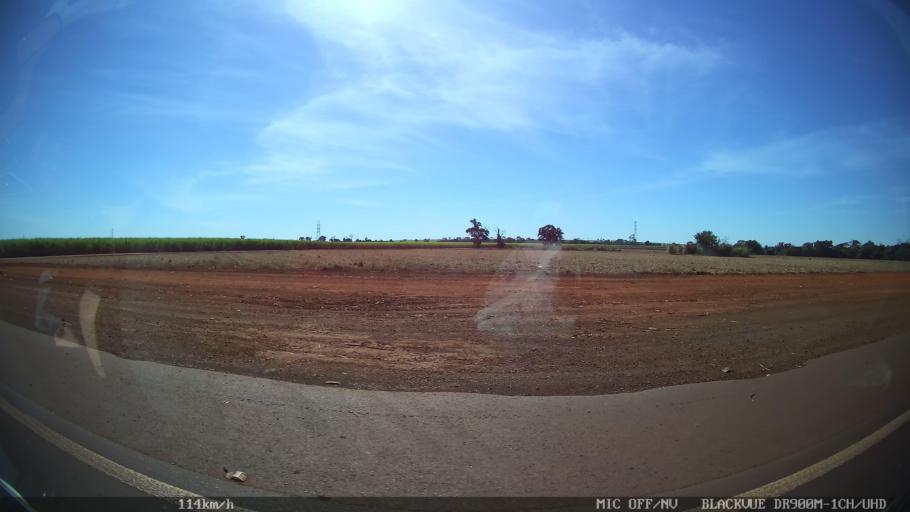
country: BR
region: Sao Paulo
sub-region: Guaira
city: Guaira
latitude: -20.4434
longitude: -48.3369
